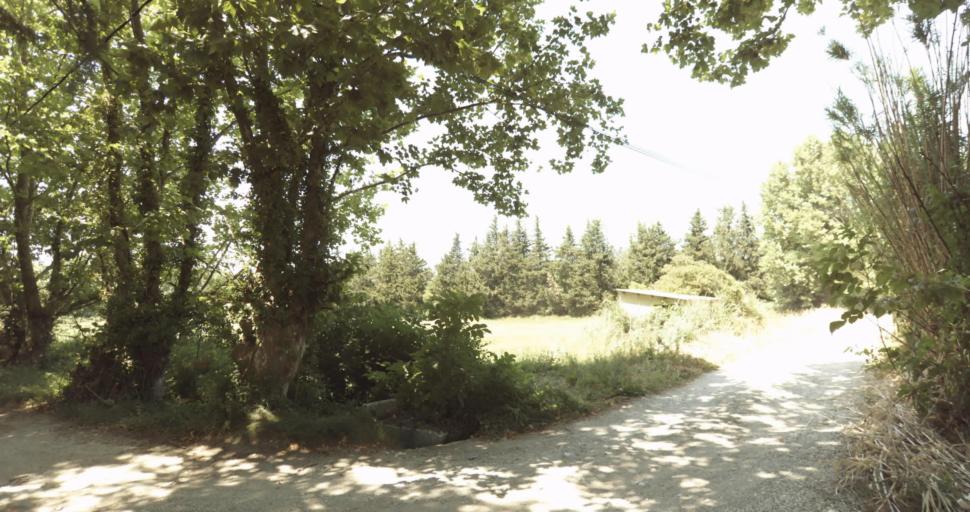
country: FR
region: Provence-Alpes-Cote d'Azur
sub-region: Departement du Vaucluse
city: Monteux
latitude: 44.0099
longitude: 5.0080
